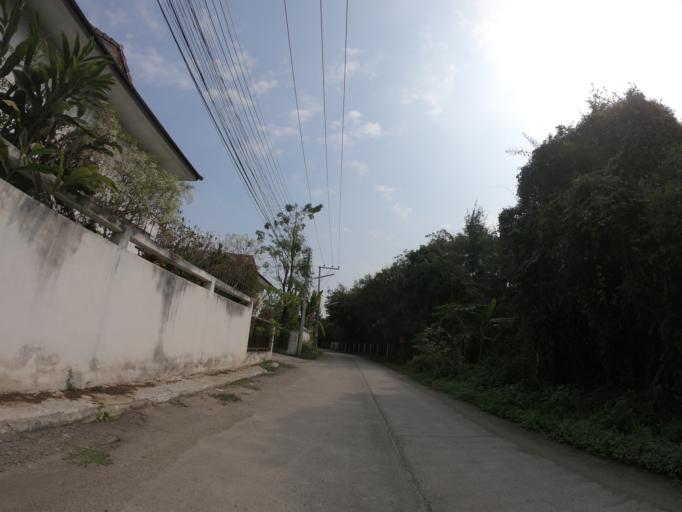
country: TH
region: Chiang Mai
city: Chiang Mai
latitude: 18.7571
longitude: 98.9777
